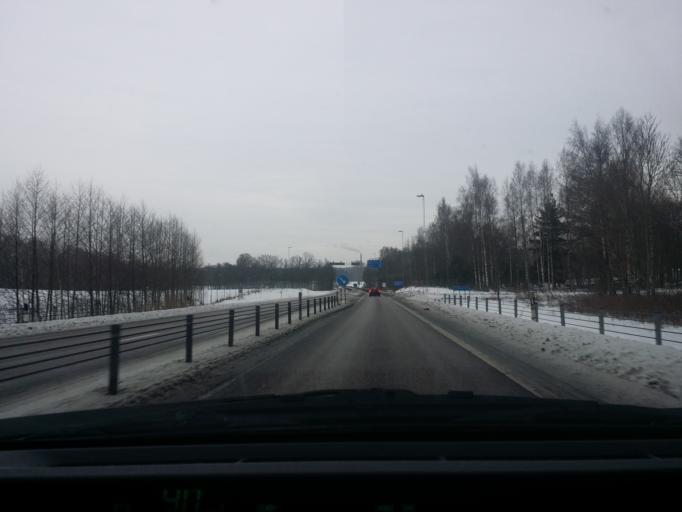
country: SE
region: Vaestra Goetaland
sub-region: Skovde Kommun
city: Stopen
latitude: 58.4527
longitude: 13.8489
